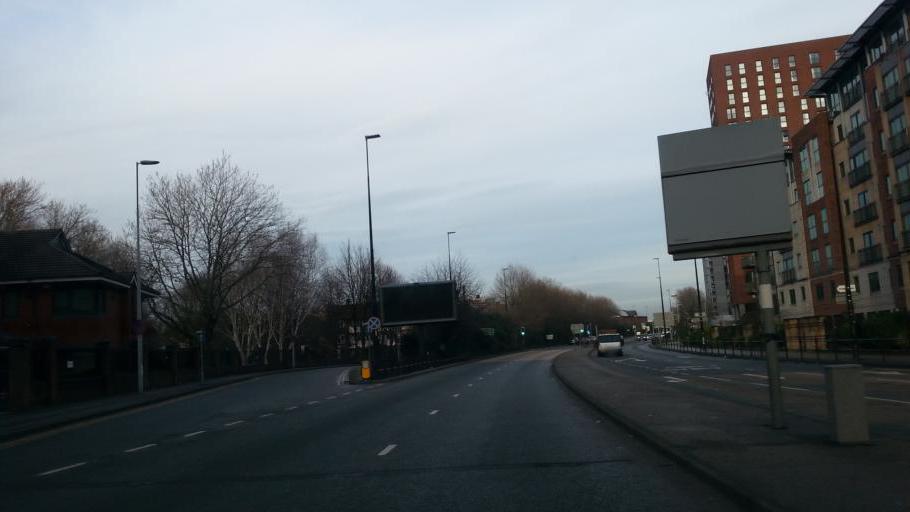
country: GB
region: England
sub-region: Manchester
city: Hulme
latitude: 53.4838
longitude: -2.2572
